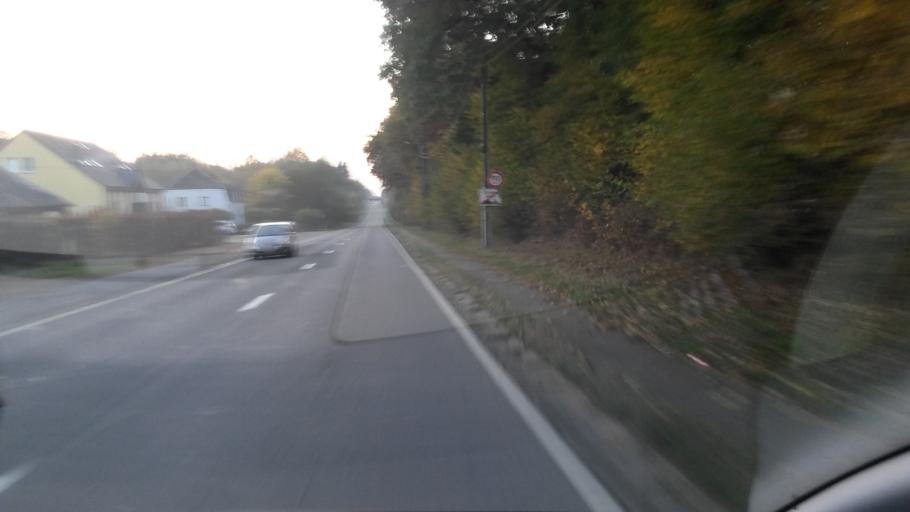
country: BE
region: Wallonia
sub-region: Province du Luxembourg
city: Arlon
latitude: 49.6865
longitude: 5.7611
